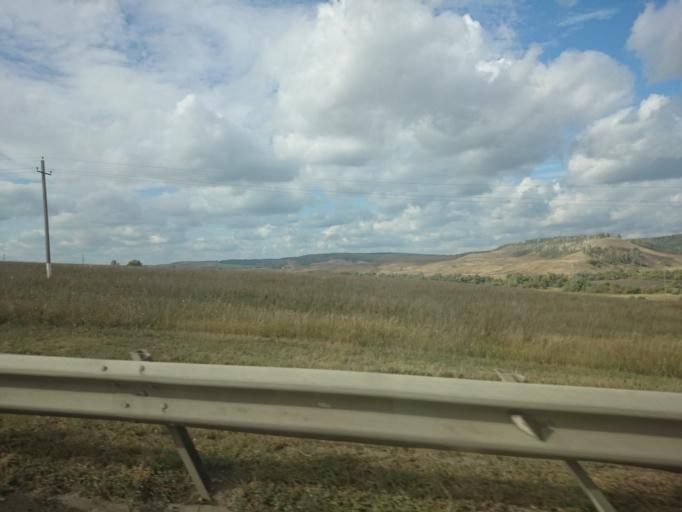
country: RU
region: Samara
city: Kamyshla
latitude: 54.0718
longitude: 52.2023
